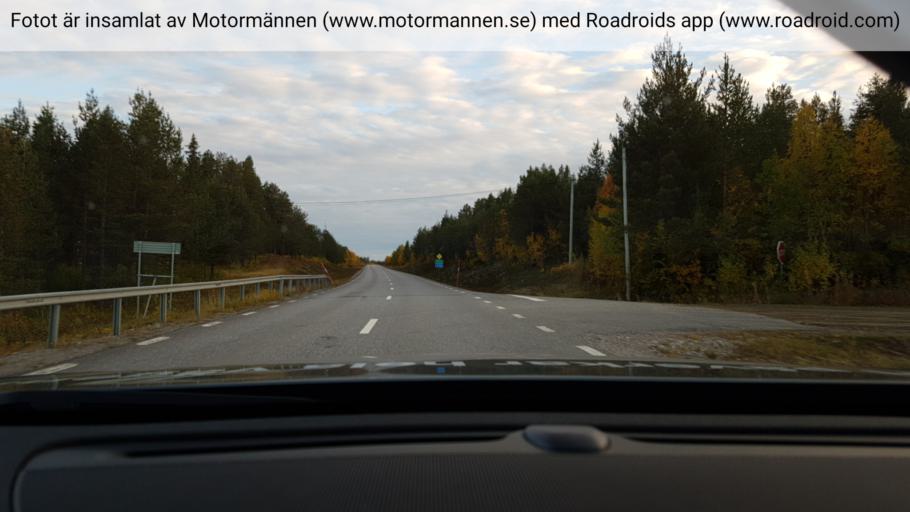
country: SE
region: Norrbotten
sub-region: Jokkmokks Kommun
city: Jokkmokk
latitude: 66.4238
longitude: 19.6823
